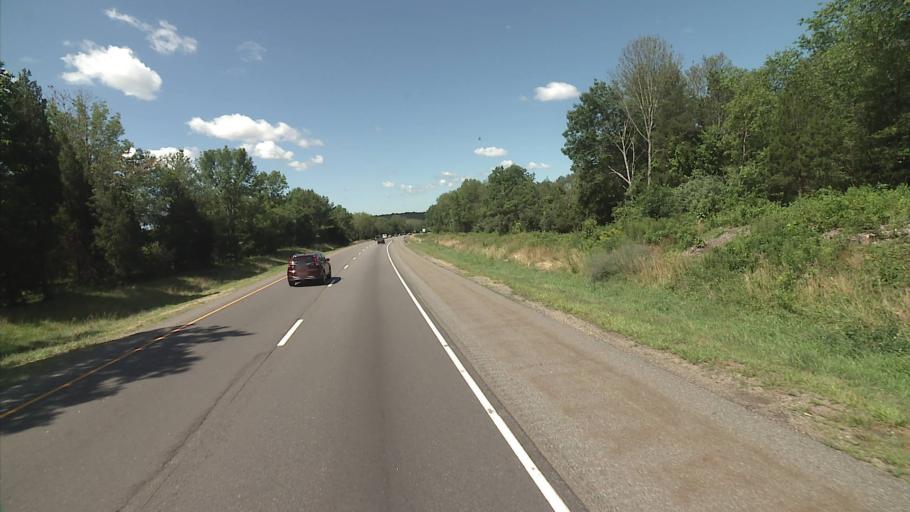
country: US
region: Rhode Island
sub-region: Washington County
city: Ashaway
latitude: 41.4306
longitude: -71.8151
